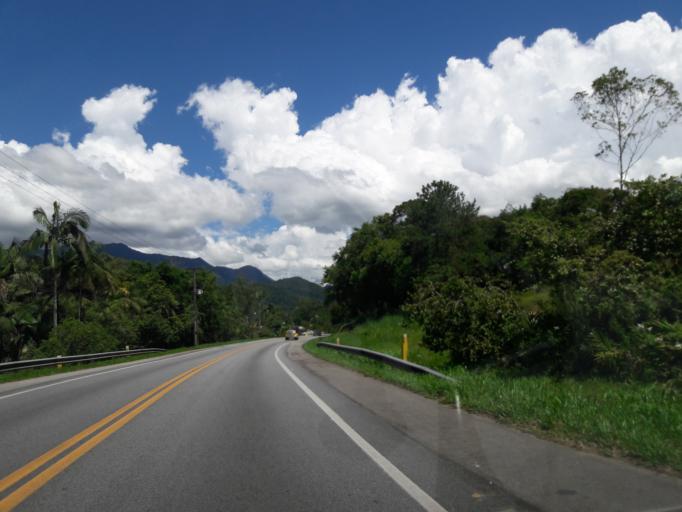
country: BR
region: Parana
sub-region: Antonina
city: Antonina
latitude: -25.5359
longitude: -48.7938
